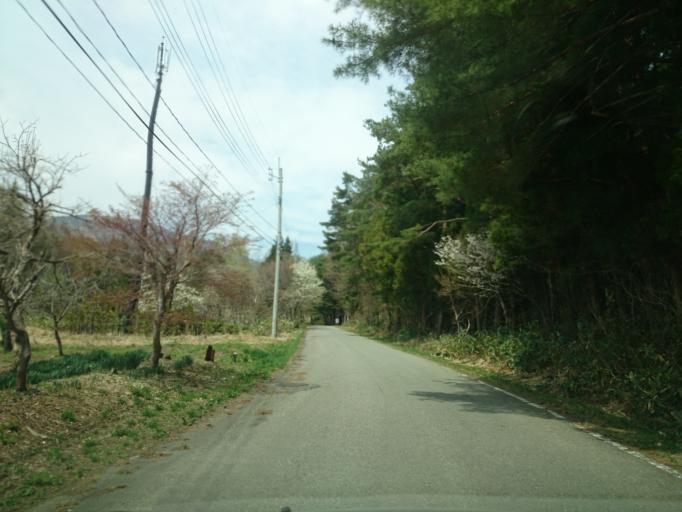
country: JP
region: Fukushima
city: Inawashiro
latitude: 37.5734
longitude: 140.1008
